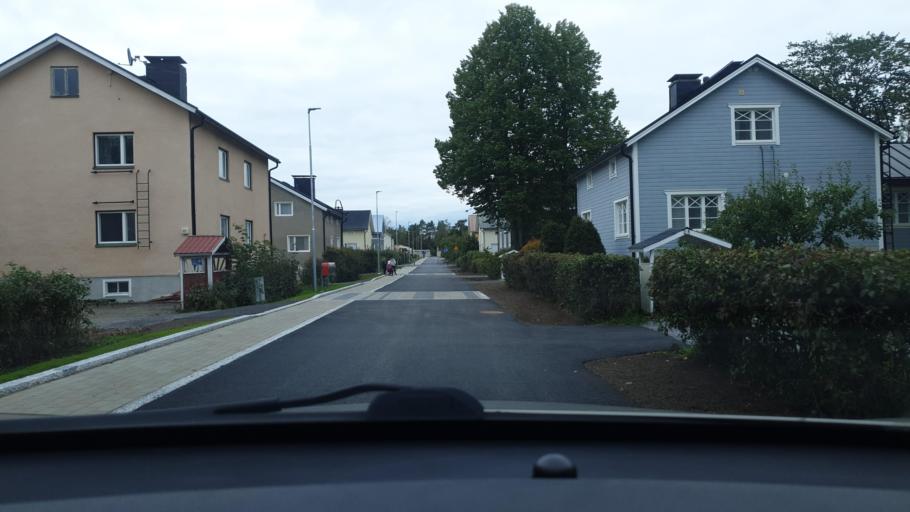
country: FI
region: Ostrobothnia
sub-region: Vaasa
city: Korsholm
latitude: 63.0949
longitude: 21.6745
